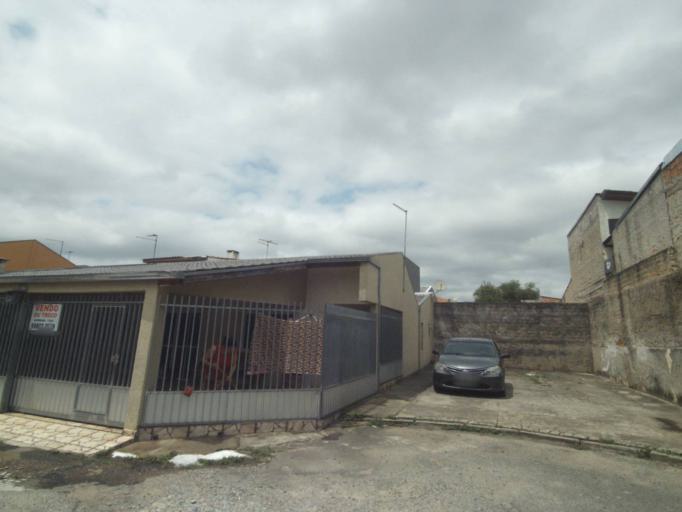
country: BR
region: Parana
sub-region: Sao Jose Dos Pinhais
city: Sao Jose dos Pinhais
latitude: -25.5385
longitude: -49.2699
